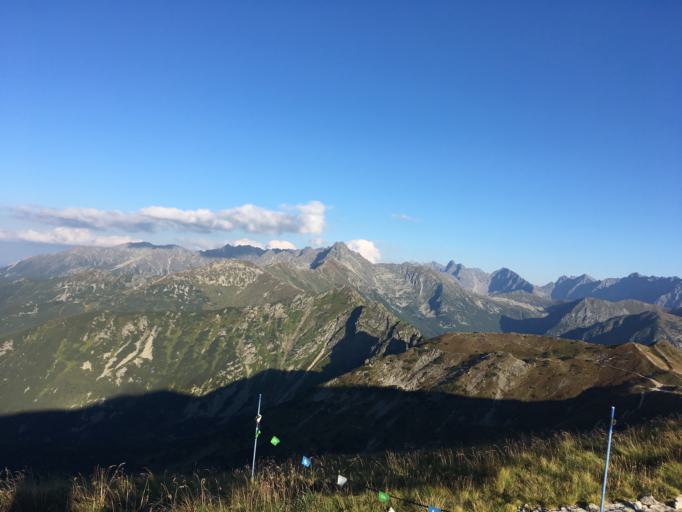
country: PL
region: Lesser Poland Voivodeship
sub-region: Powiat tatrzanski
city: Zakopane
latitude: 49.2384
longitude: 19.9338
